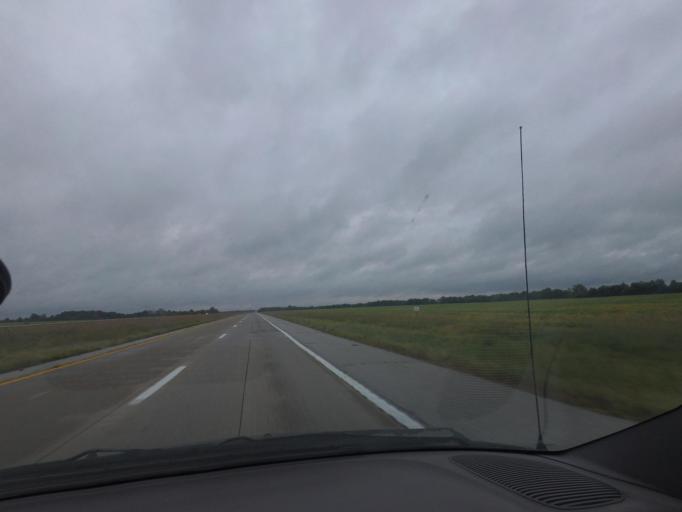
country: US
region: Missouri
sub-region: Marion County
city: Monroe City
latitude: 39.6582
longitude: -91.7871
